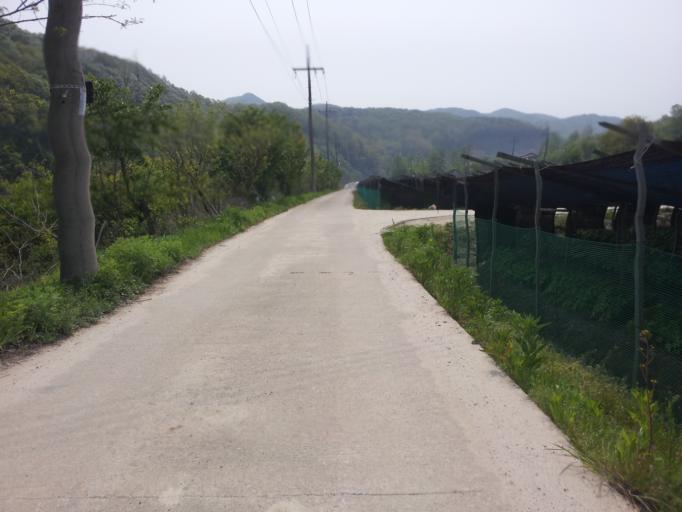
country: KR
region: Daejeon
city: Daejeon
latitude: 36.2697
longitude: 127.3406
